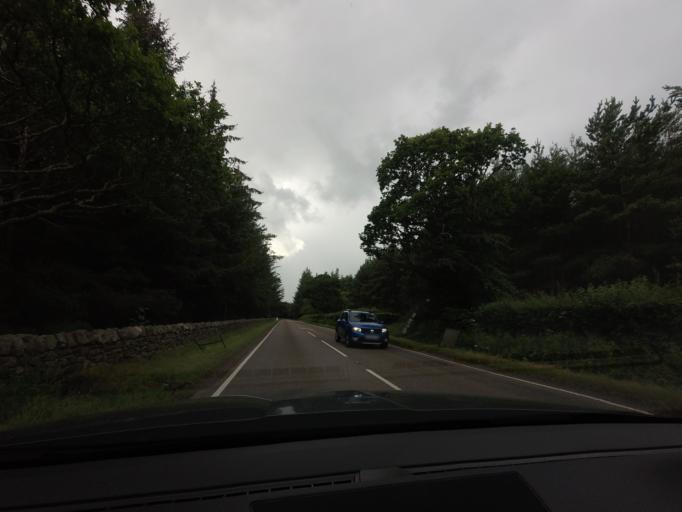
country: GB
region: Scotland
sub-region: Moray
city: Findochty
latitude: 57.6819
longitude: -2.8897
